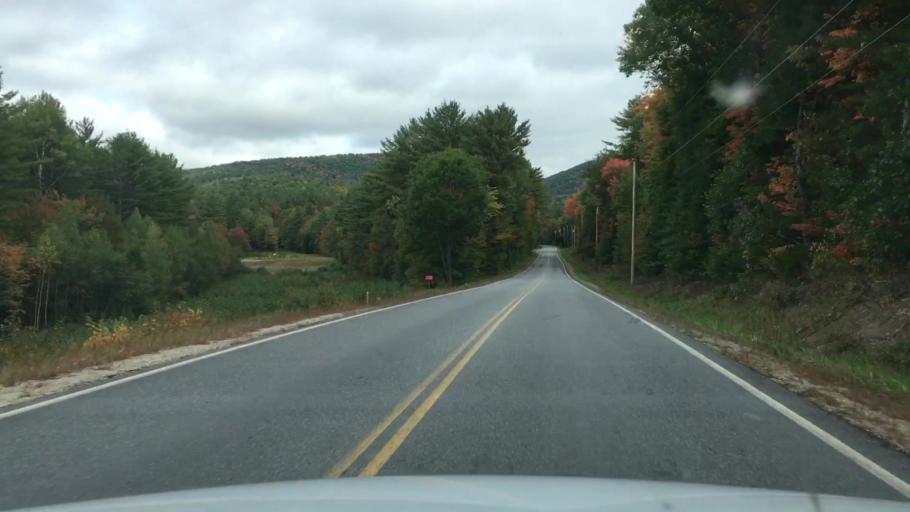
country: US
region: Maine
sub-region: Oxford County
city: Bethel
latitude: 44.2650
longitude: -70.7273
